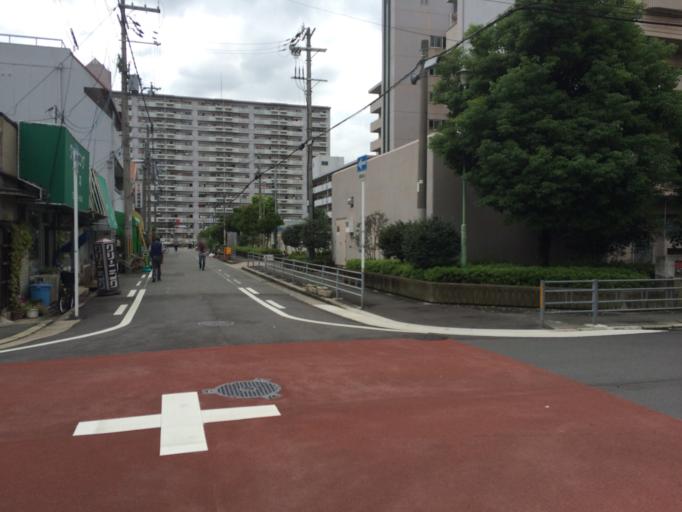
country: JP
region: Osaka
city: Sakai
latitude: 34.5953
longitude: 135.5102
